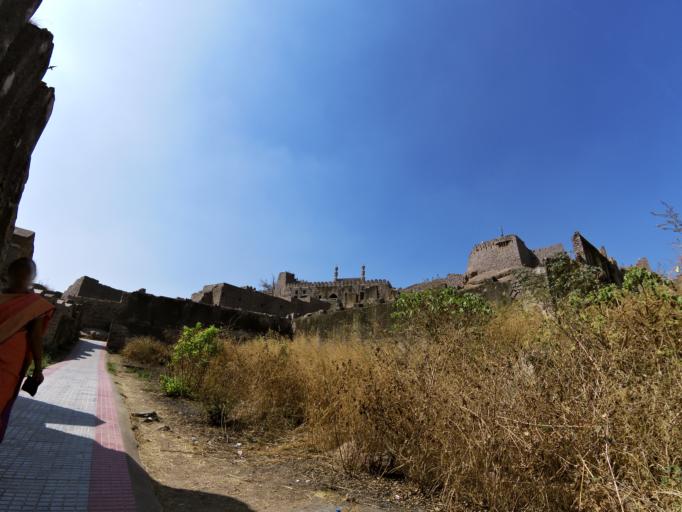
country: IN
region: Telangana
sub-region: Hyderabad
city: Hyderabad
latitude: 17.3841
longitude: 78.4010
